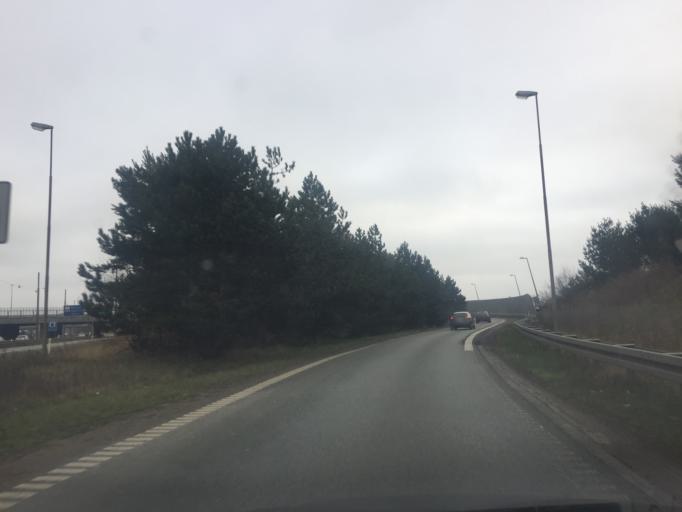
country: DK
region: Capital Region
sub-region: Herlev Kommune
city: Herlev
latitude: 55.7424
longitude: 12.4547
